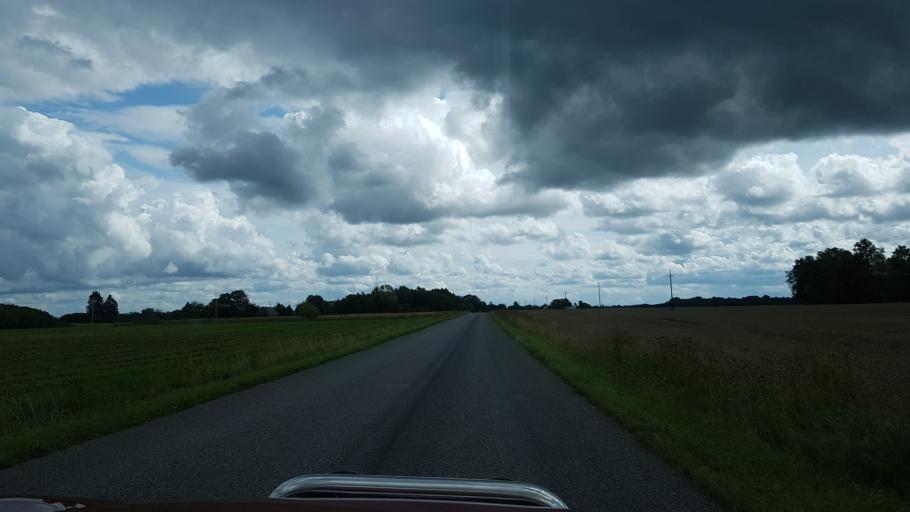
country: EE
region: Laeaene
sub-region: Lihula vald
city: Lihula
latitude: 58.7154
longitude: 23.9964
